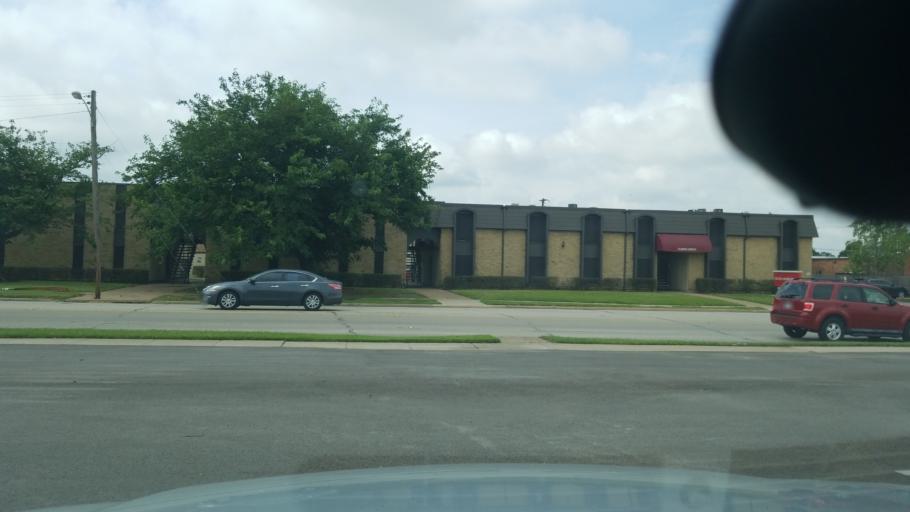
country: US
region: Texas
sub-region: Dallas County
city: Irving
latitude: 32.8444
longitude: -96.9580
